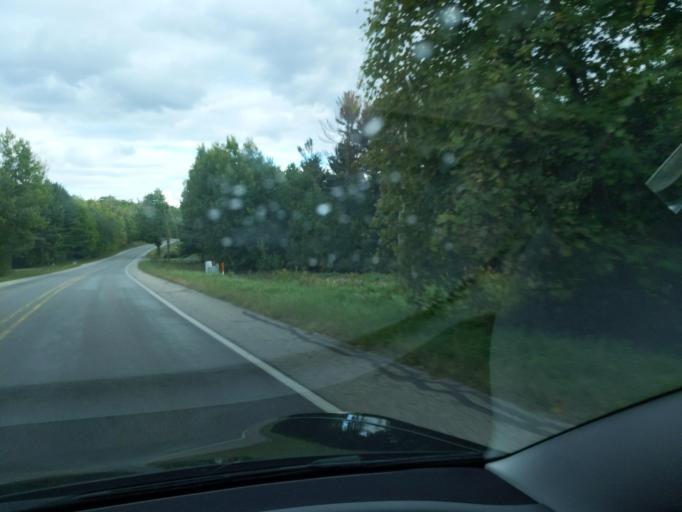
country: US
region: Michigan
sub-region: Kalkaska County
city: Rapid City
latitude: 44.8025
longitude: -85.2748
